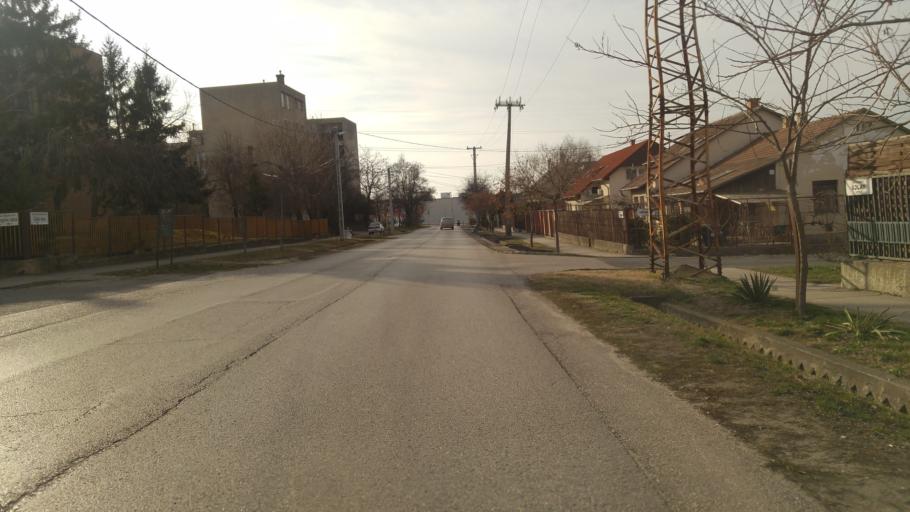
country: HU
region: Budapest
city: Budapest XVII. keruelet
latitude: 47.4822
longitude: 19.2315
